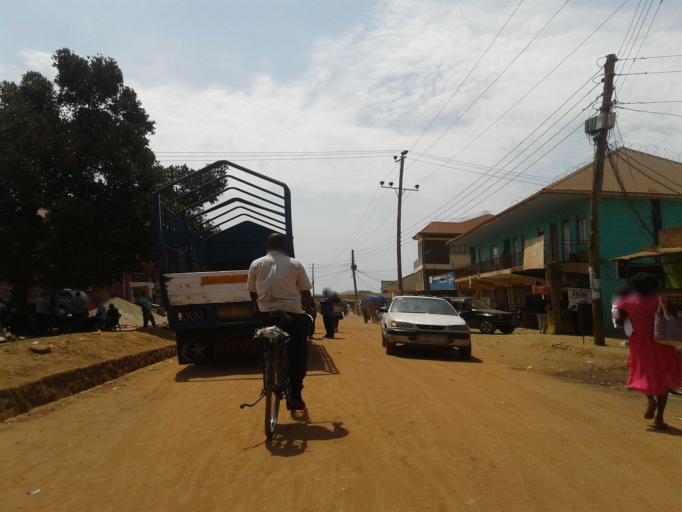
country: UG
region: Central Region
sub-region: Kampala District
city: Kampala
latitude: 0.2575
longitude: 32.6352
